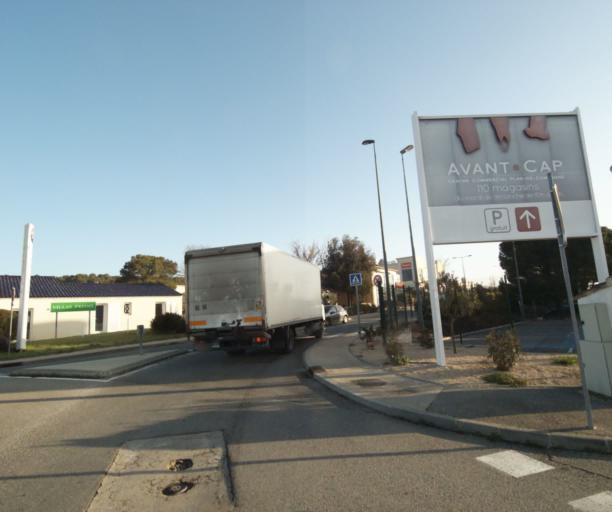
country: FR
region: Provence-Alpes-Cote d'Azur
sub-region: Departement des Bouches-du-Rhone
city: Septemes-les-Vallons
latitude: 43.4201
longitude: 5.3596
